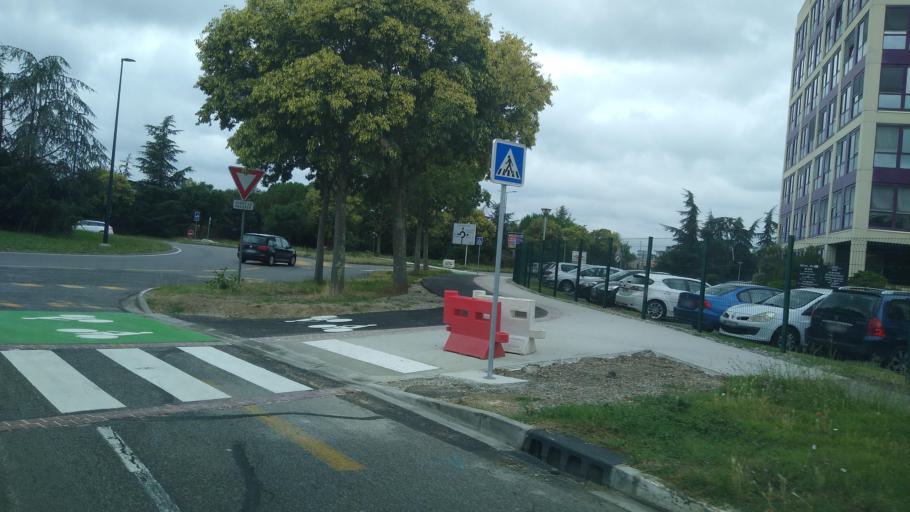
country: FR
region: Midi-Pyrenees
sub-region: Departement de la Haute-Garonne
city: Blagnac
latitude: 43.5790
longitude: 1.3945
